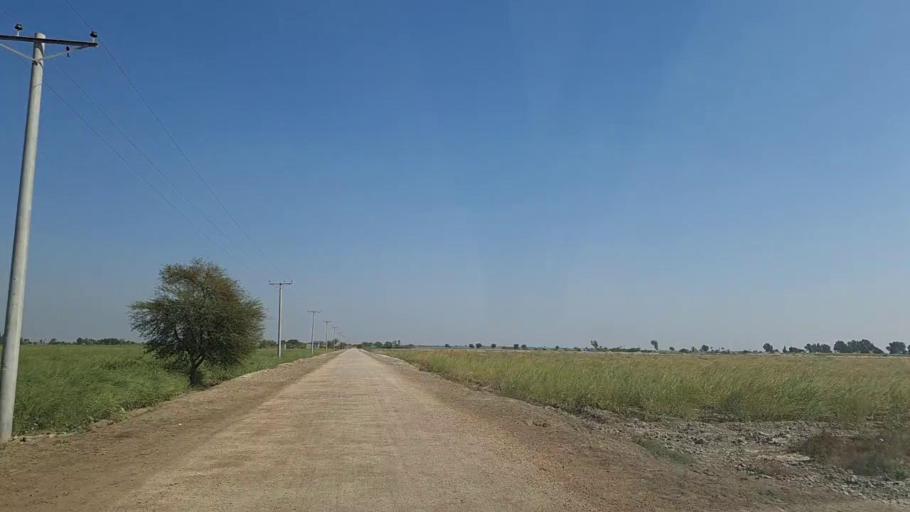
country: PK
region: Sindh
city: Pithoro
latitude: 25.4165
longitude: 69.4111
